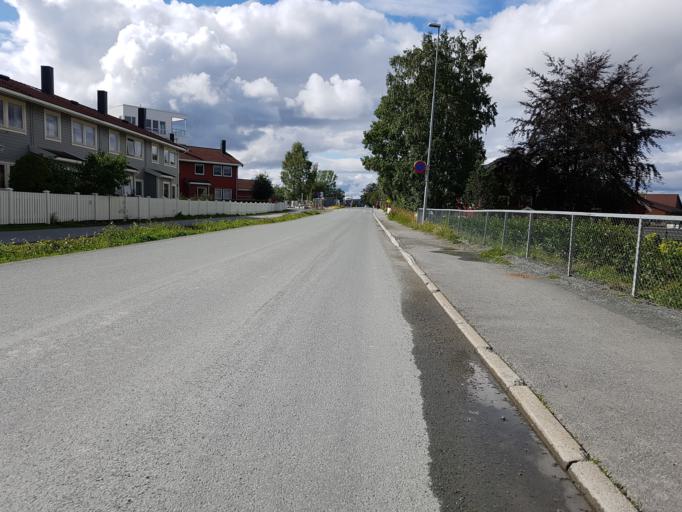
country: NO
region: Sor-Trondelag
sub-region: Trondheim
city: Trondheim
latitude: 63.4127
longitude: 10.4715
